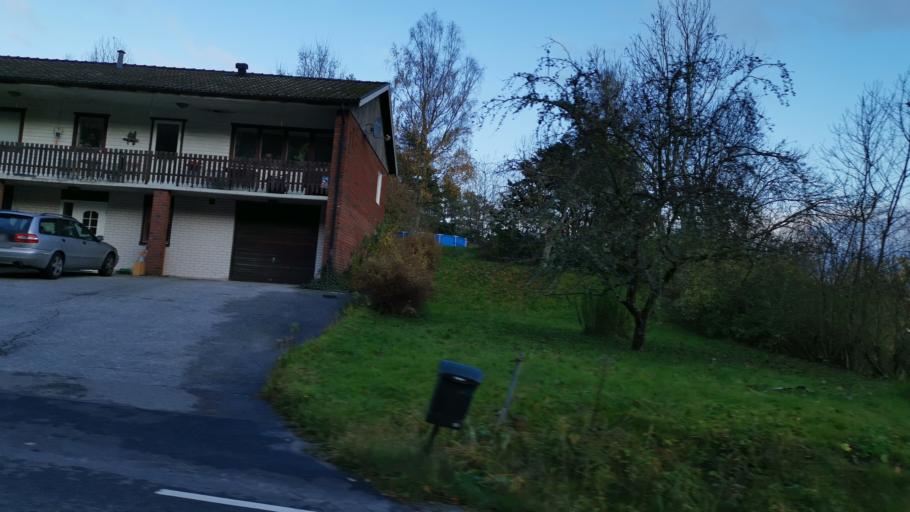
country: SE
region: Vaestra Goetaland
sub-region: Munkedals Kommun
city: Munkedal
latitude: 58.4929
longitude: 11.6948
